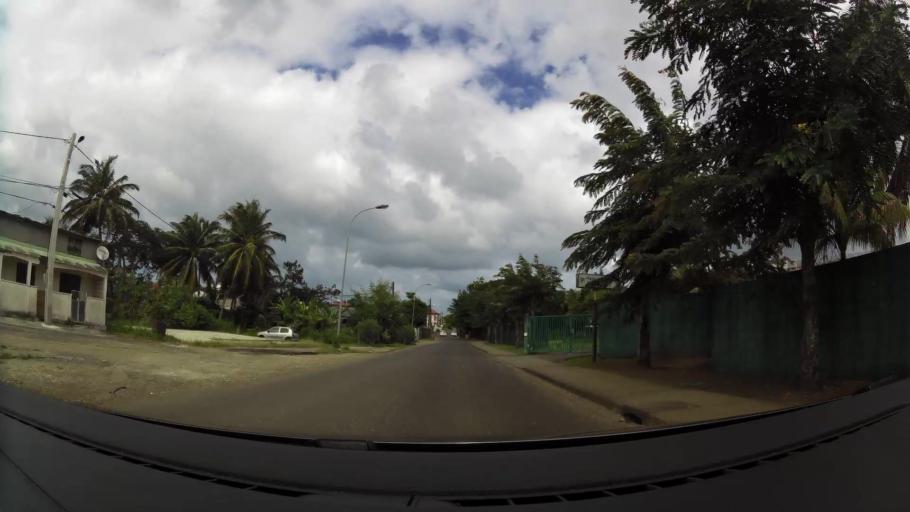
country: GP
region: Guadeloupe
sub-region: Guadeloupe
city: Baie-Mahault
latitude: 16.2663
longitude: -61.5834
